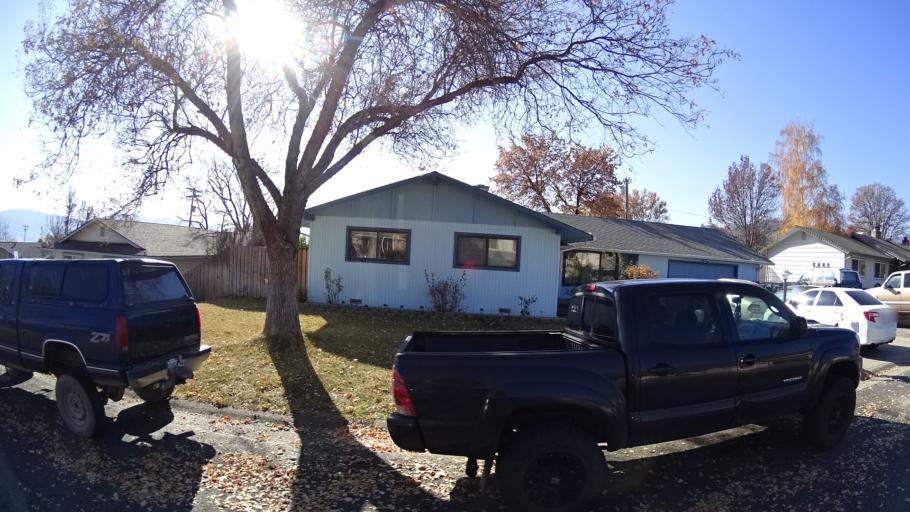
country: US
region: California
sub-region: Siskiyou County
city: Yreka
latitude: 41.7422
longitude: -122.6483
